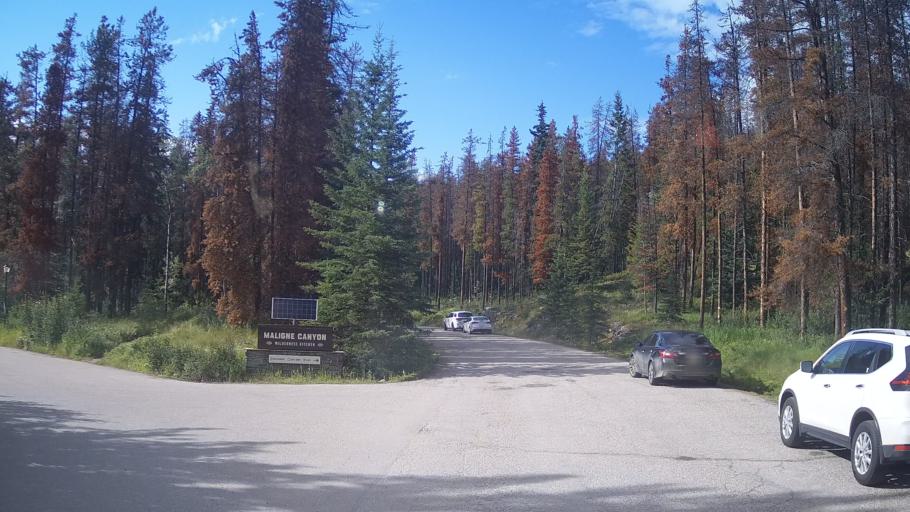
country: CA
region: Alberta
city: Jasper Park Lodge
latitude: 52.9202
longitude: -117.9967
